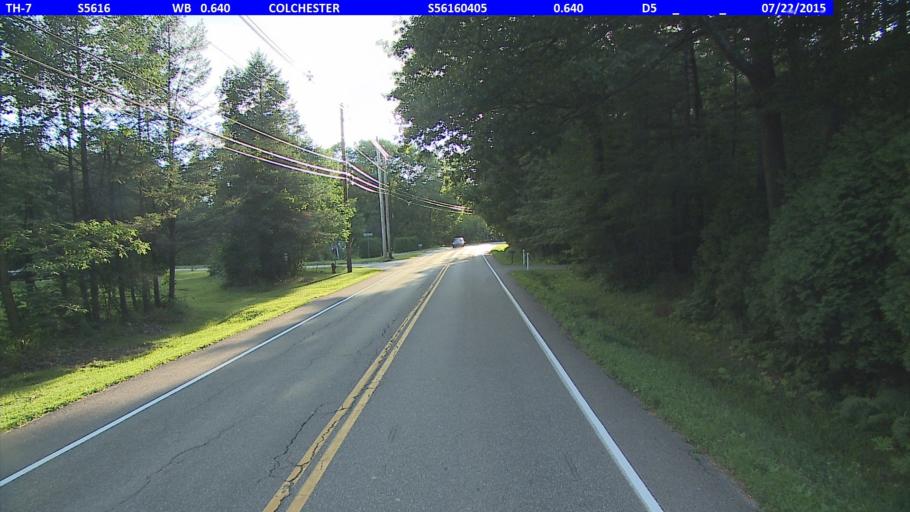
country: US
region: Vermont
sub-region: Chittenden County
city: Colchester
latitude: 44.5248
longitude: -73.1608
